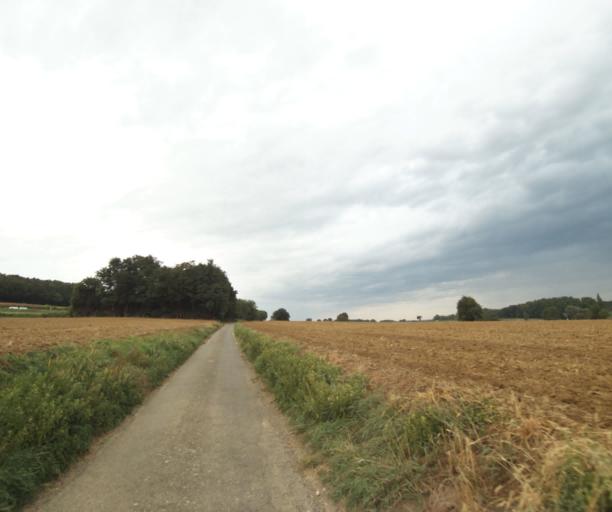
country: FR
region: Bourgogne
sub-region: Departement de Saone-et-Loire
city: Tournus
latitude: 46.5915
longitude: 4.9084
